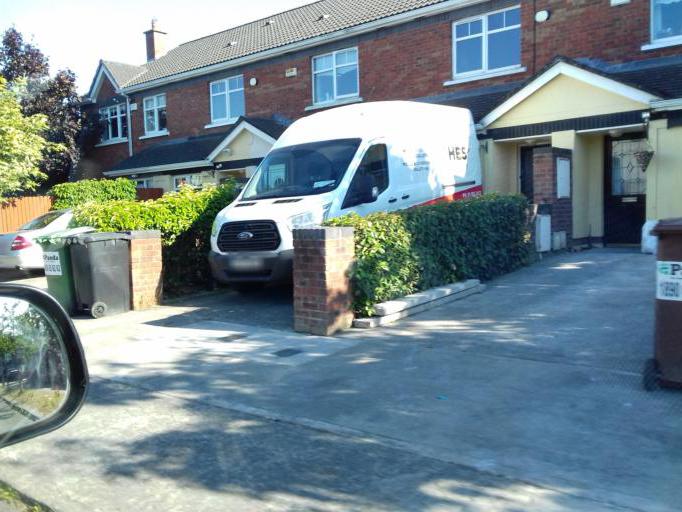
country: IE
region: Leinster
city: Hartstown
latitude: 53.3910
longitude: -6.4262
